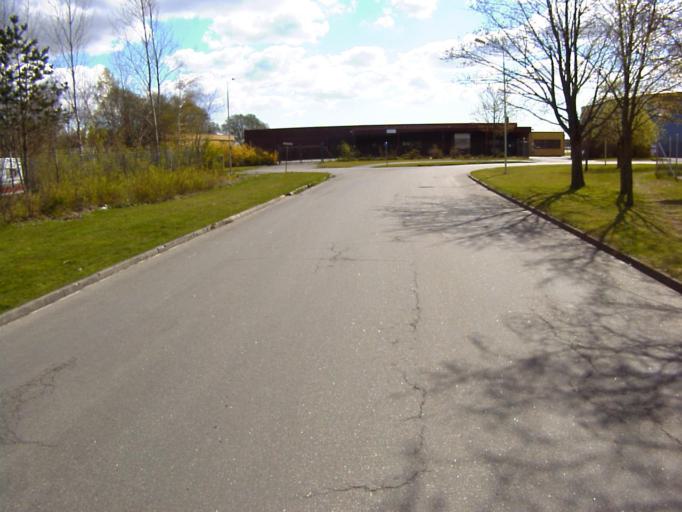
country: SE
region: Skane
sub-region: Kristianstads Kommun
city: Norra Asum
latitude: 56.0081
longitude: 14.1040
